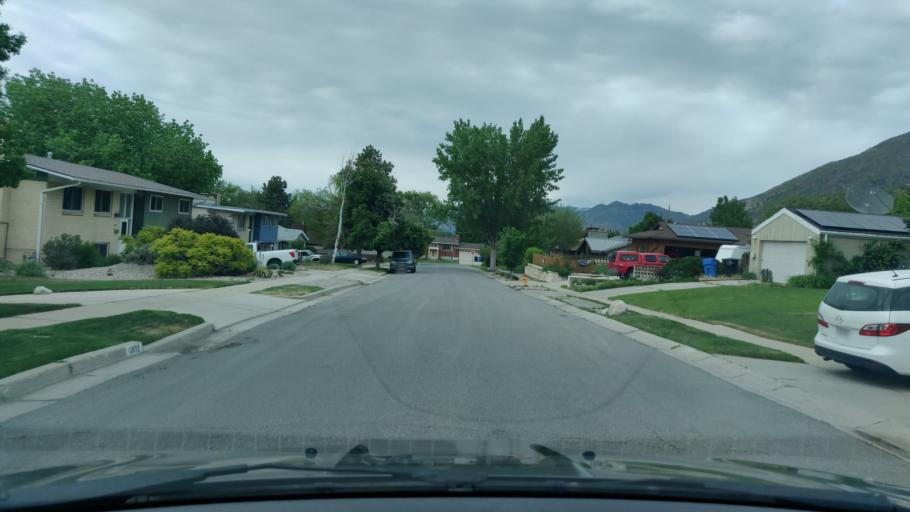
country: US
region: Utah
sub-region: Salt Lake County
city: Cottonwood Heights
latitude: 40.6260
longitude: -111.8199
